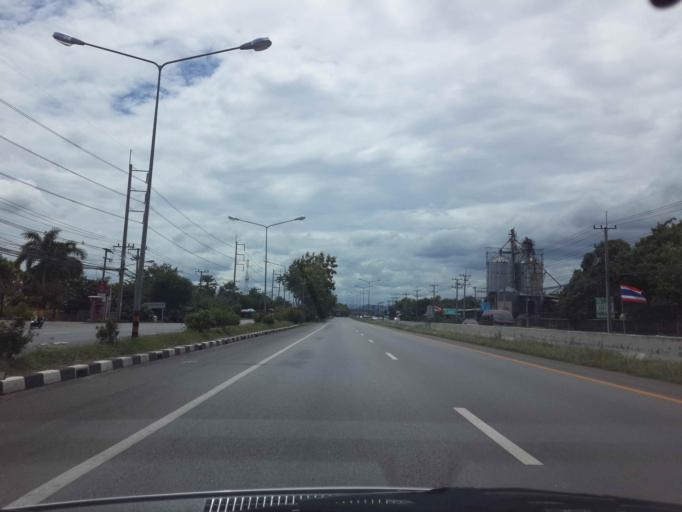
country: TH
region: Phetchaburi
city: Phetchaburi
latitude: 13.1175
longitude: 99.9086
